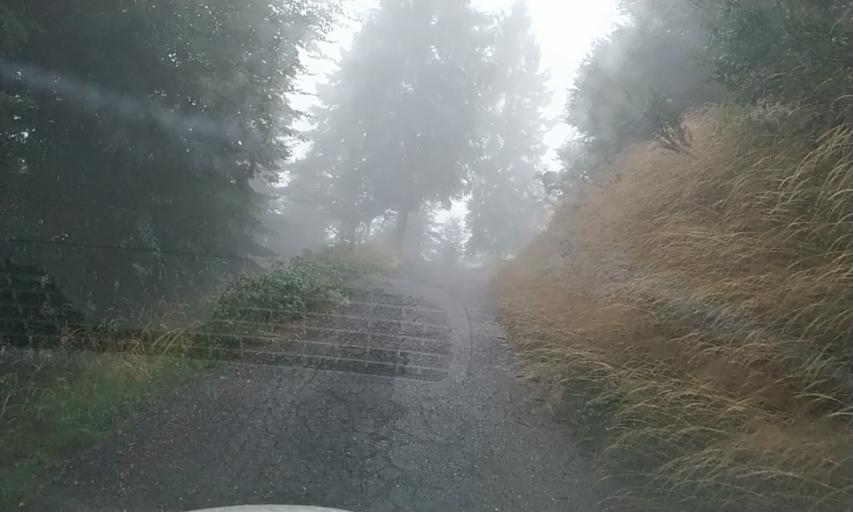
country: IT
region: Piedmont
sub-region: Provincia di Vercelli
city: Civiasco
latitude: 45.8348
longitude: 8.3187
